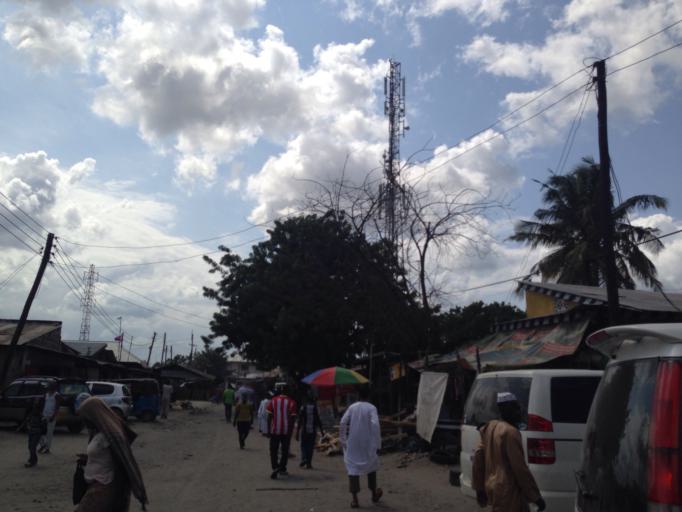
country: TZ
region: Dar es Salaam
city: Dar es Salaam
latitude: -6.8426
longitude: 39.2805
